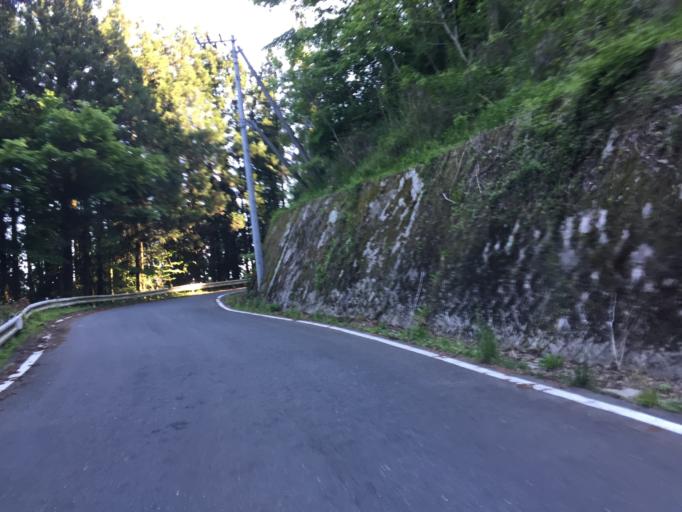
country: JP
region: Ibaraki
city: Kitaibaraki
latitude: 36.9182
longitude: 140.5790
